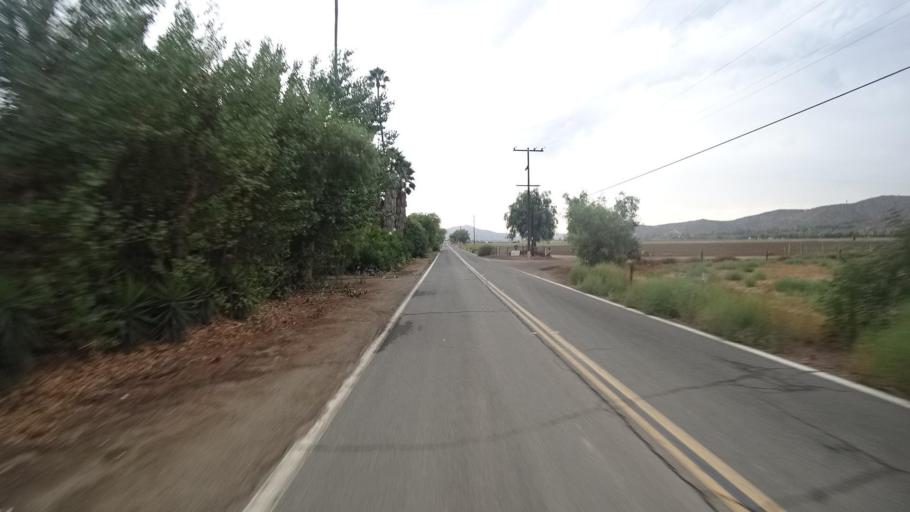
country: US
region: California
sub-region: San Diego County
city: San Pasqual
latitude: 33.0838
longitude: -116.9632
